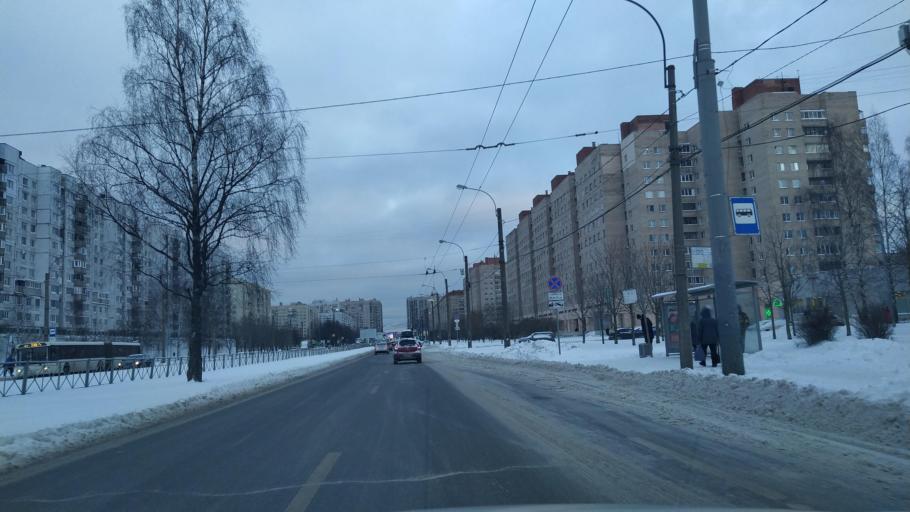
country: RU
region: St.-Petersburg
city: Komendantsky aerodrom
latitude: 59.9985
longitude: 30.2771
